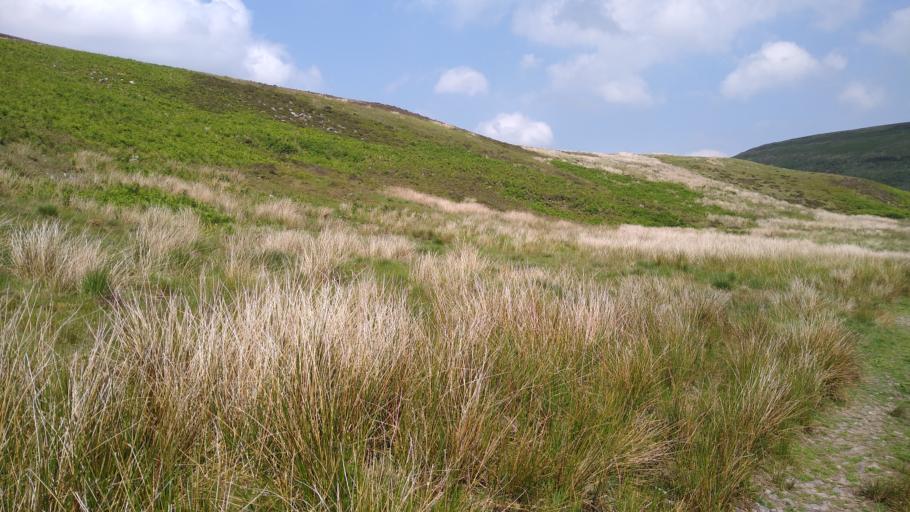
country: GB
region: England
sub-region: Cumbria
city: Brampton
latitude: 54.8936
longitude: -2.6536
